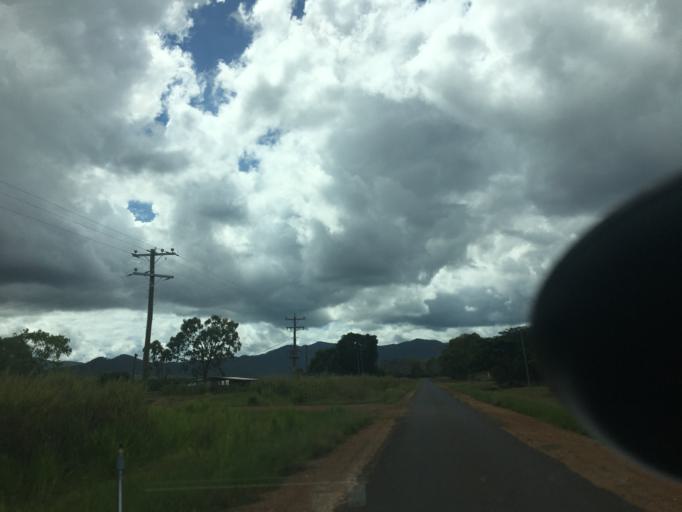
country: AU
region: Queensland
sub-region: Tablelands
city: Mareeba
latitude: -16.9962
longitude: 145.5231
